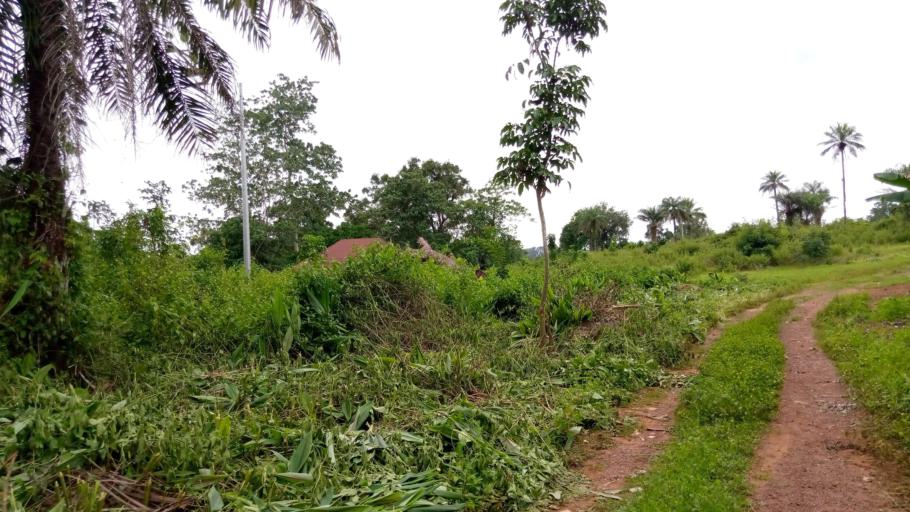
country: SL
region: Southern Province
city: Rotifunk
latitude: 8.1896
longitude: -12.5653
